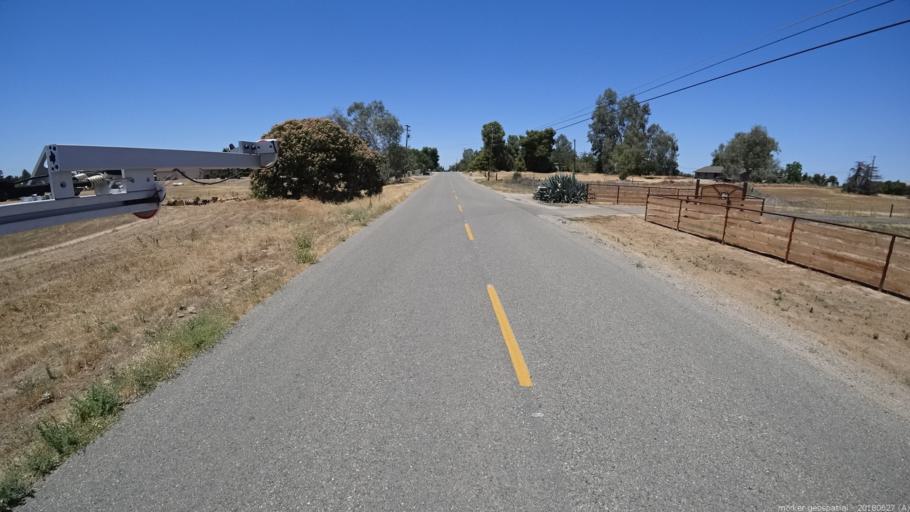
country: US
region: California
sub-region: Madera County
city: Bonadelle Ranchos-Madera Ranchos
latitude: 36.9410
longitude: -119.9046
